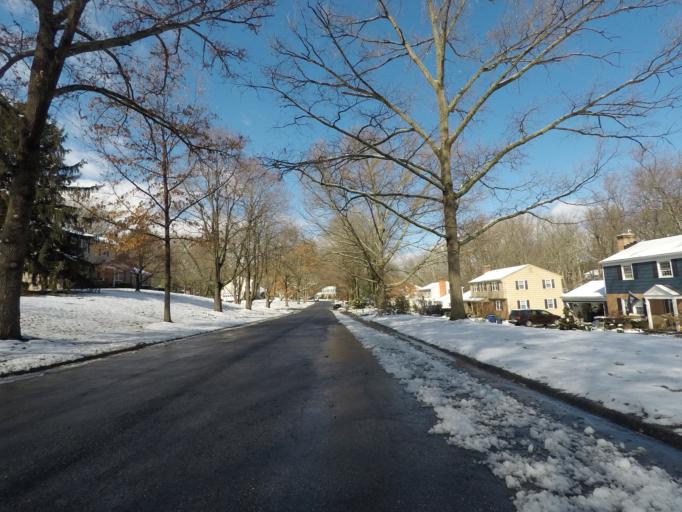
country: US
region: Maryland
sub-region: Howard County
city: Columbia
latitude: 39.2704
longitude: -76.8547
